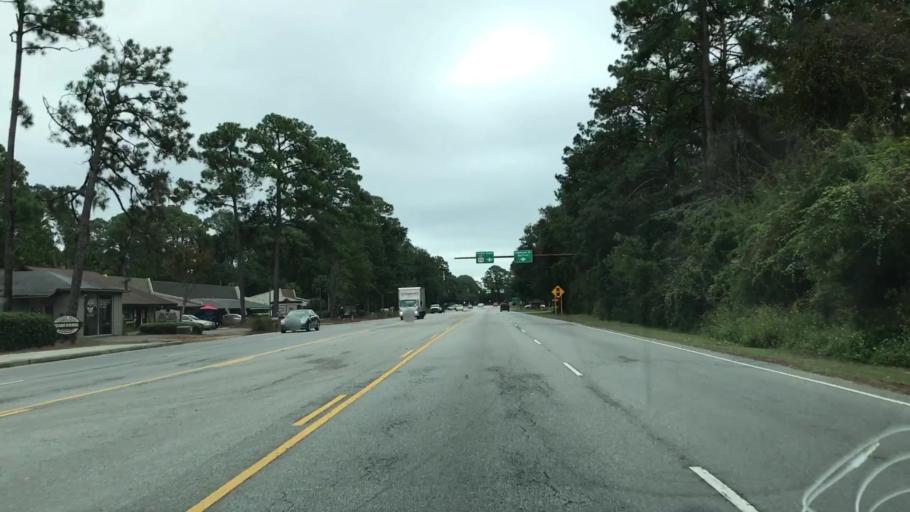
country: US
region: South Carolina
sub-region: Beaufort County
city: Hilton Head Island
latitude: 32.1599
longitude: -80.7664
